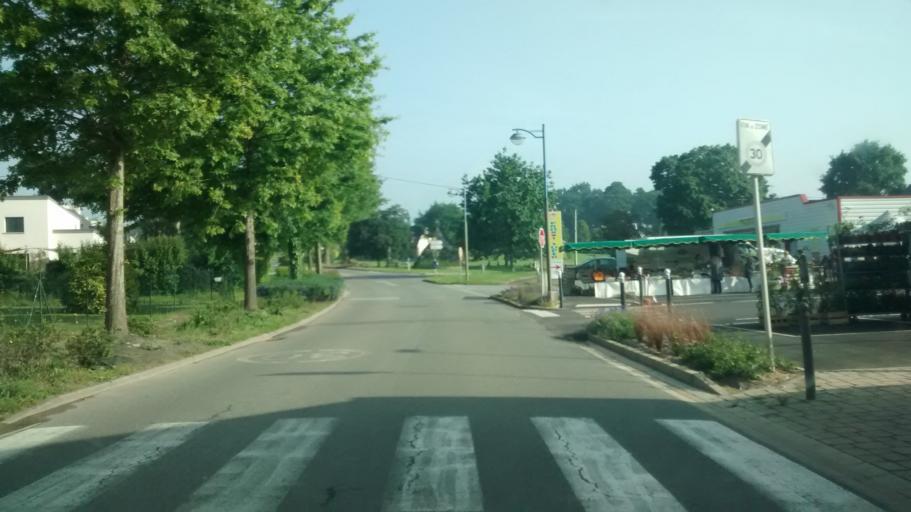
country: FR
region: Brittany
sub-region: Departement du Morbihan
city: Ruffiac
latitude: 47.8194
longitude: -2.2826
